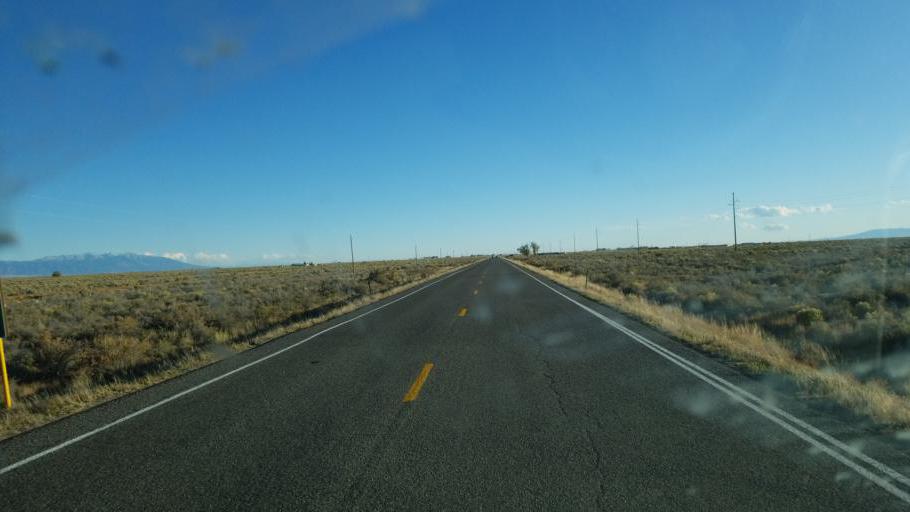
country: US
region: Colorado
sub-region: Saguache County
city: Saguache
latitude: 38.0926
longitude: -105.9189
